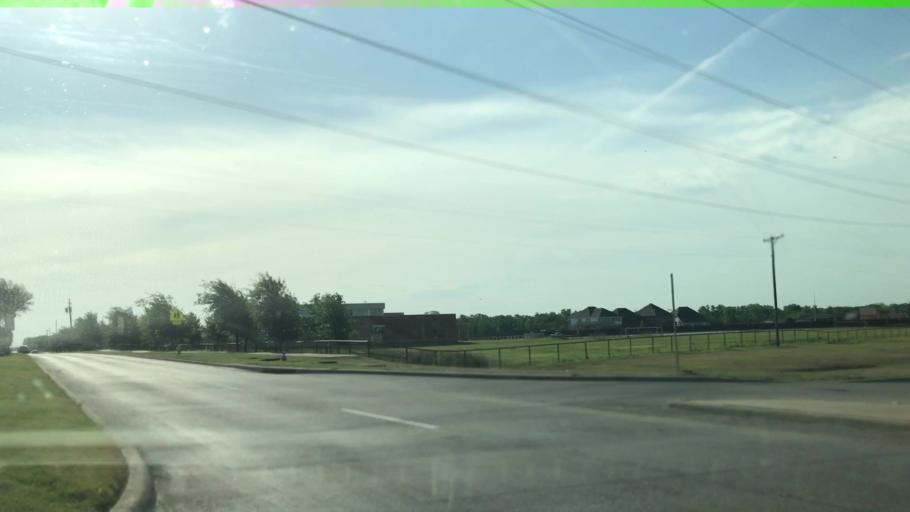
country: US
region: Texas
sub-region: Dallas County
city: Farmers Branch
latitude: 32.8957
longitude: -96.9380
